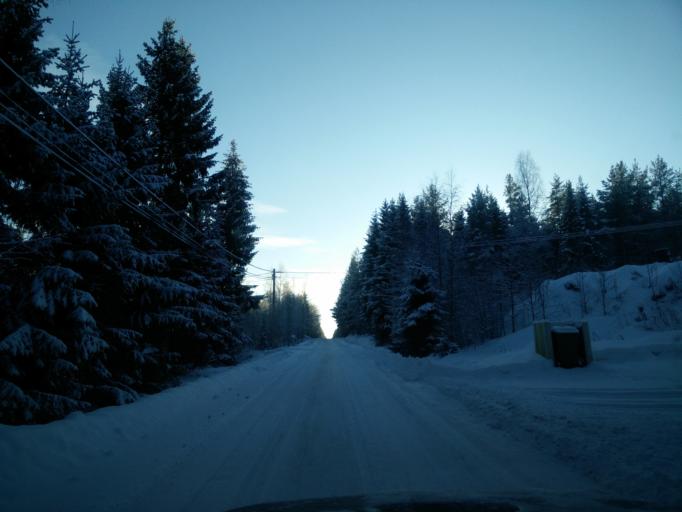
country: SE
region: Vaesternorrland
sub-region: Sundsvalls Kommun
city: Njurundabommen
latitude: 62.2191
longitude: 17.4933
